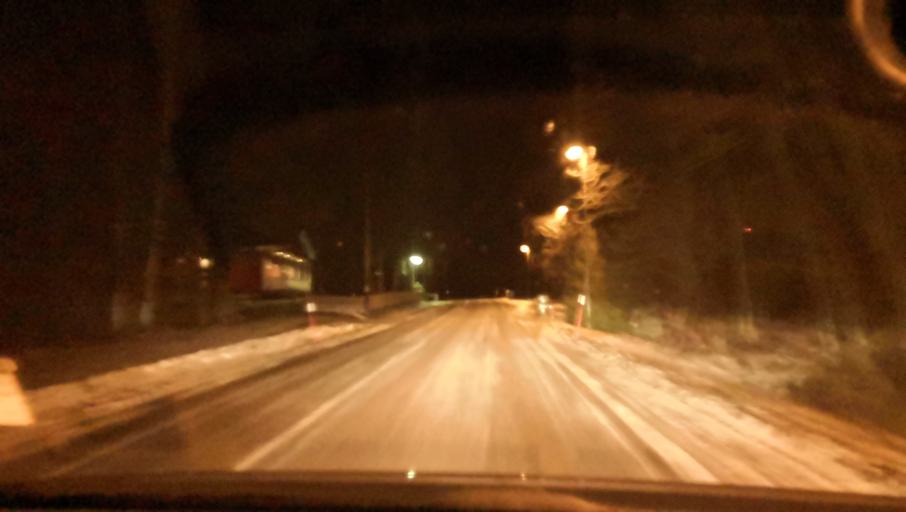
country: SE
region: Vaestmanland
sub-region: Vasteras
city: Tillberga
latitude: 59.6785
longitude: 16.7168
